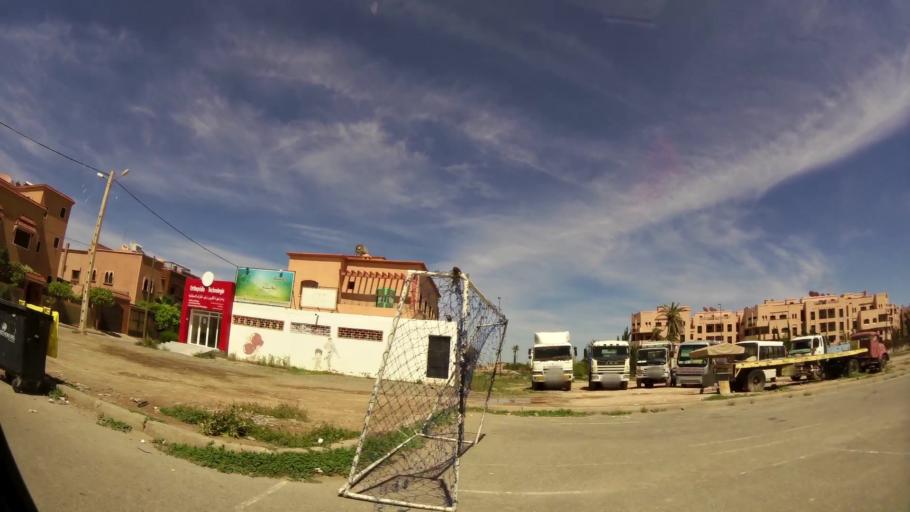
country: MA
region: Marrakech-Tensift-Al Haouz
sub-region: Marrakech
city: Marrakesh
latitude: 31.6634
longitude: -7.9916
